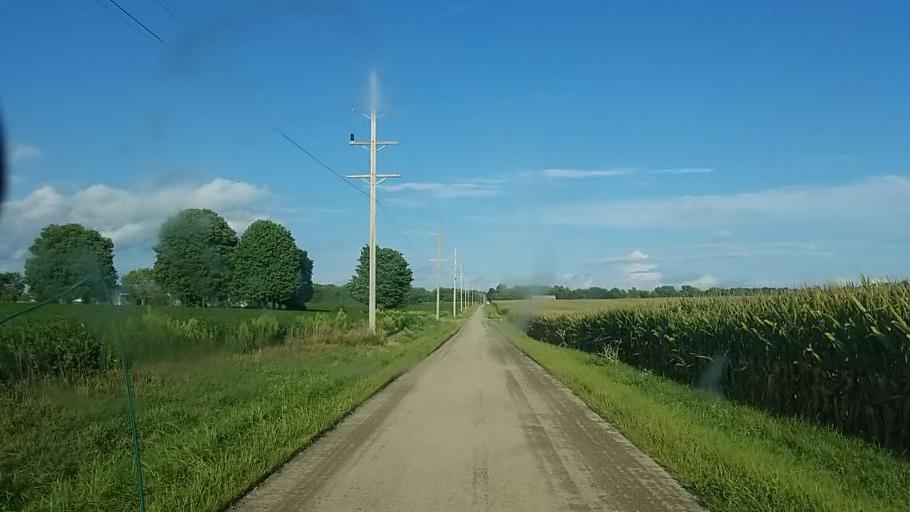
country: US
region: Ohio
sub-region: Wyandot County
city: Upper Sandusky
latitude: 40.8335
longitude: -83.1302
